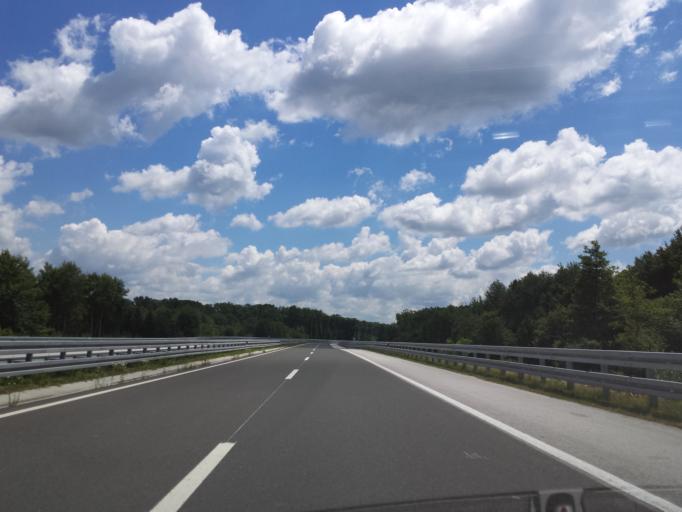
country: HR
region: Sisacko-Moslavacka
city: Lekenik
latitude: 45.5866
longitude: 16.1795
